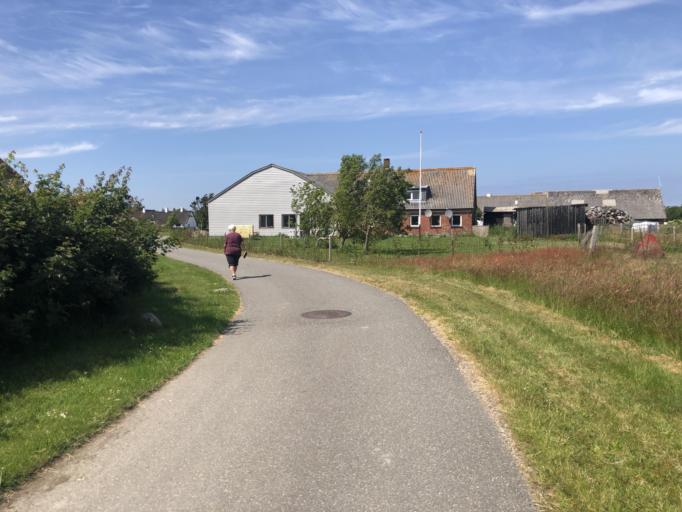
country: DK
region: South Denmark
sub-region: Esbjerg Kommune
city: Tjaereborg
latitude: 55.2726
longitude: 8.5390
